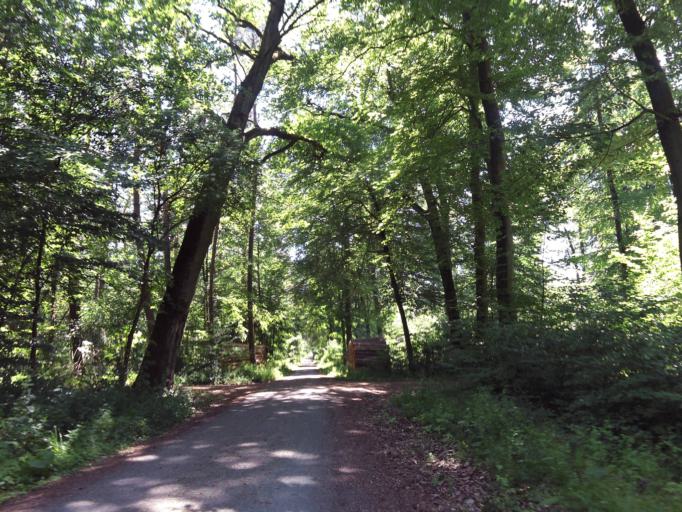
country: DE
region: Hesse
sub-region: Regierungsbezirk Darmstadt
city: Erzhausen
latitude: 49.9778
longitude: 8.6290
